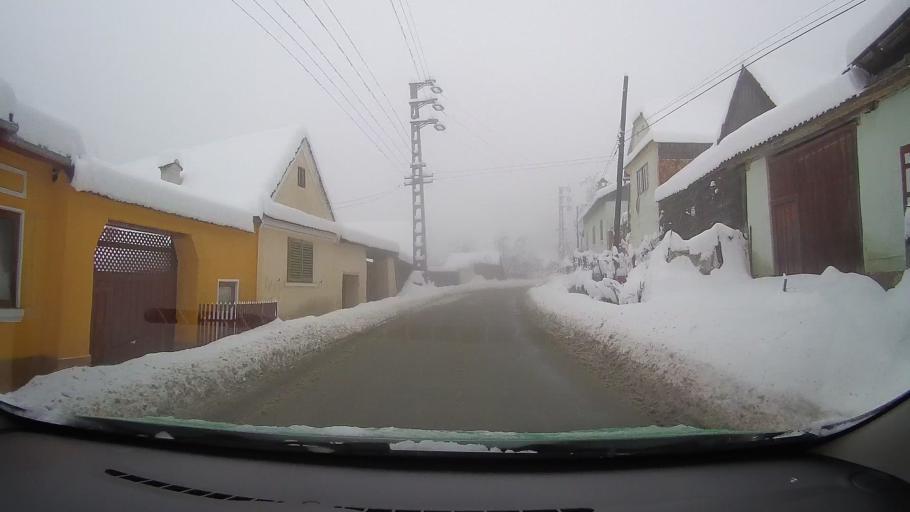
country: RO
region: Sibiu
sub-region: Comuna Poiana Sibiului
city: Poiana Sibiului
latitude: 45.8050
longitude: 23.7739
